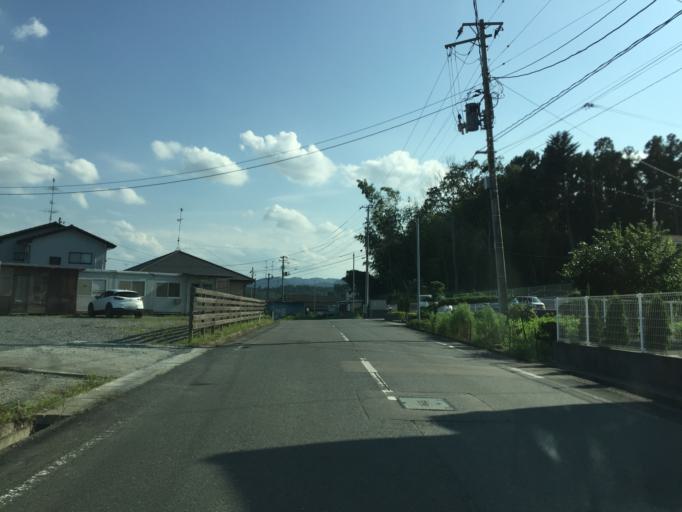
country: JP
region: Miyagi
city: Marumori
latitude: 37.8064
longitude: 140.8950
